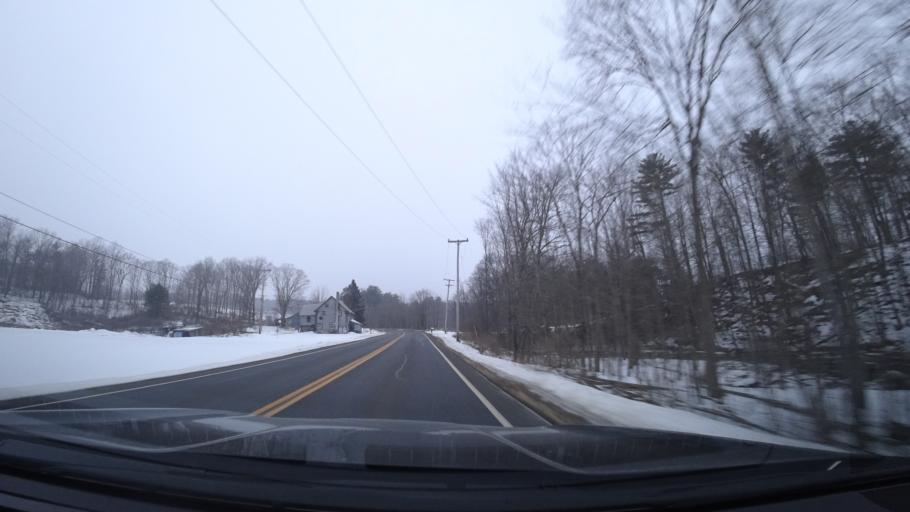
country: US
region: New York
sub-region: Washington County
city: Greenwich
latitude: 43.1557
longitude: -73.4191
